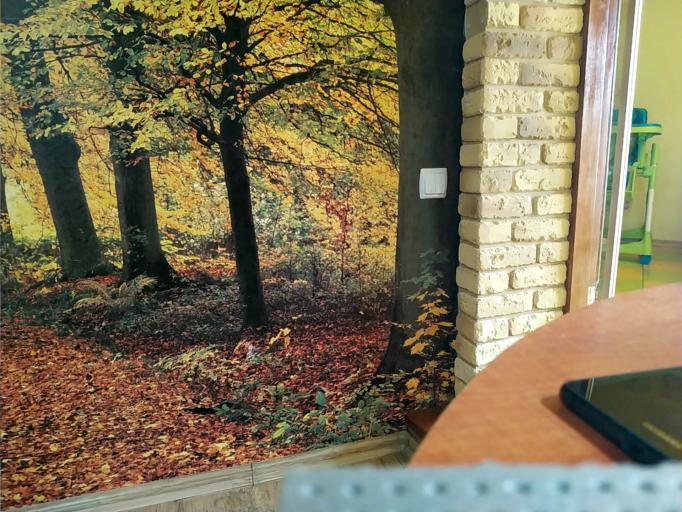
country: RU
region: Tverskaya
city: Kalashnikovo
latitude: 57.2761
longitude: 35.1184
